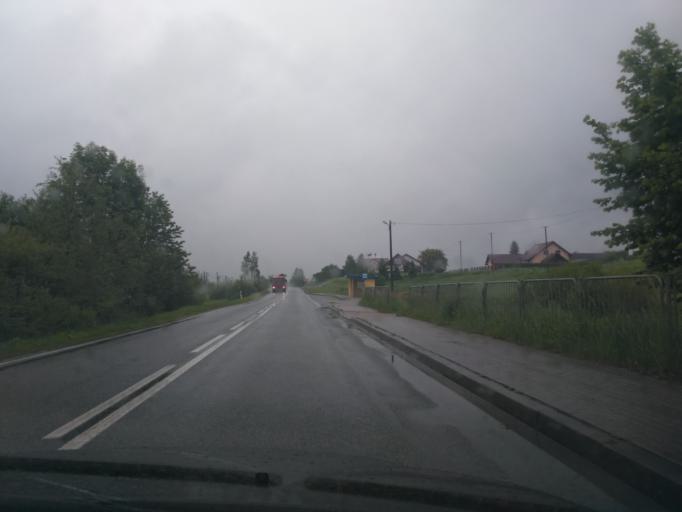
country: PL
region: Subcarpathian Voivodeship
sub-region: Powiat krosnienski
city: Leki
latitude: 49.7985
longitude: 21.6469
